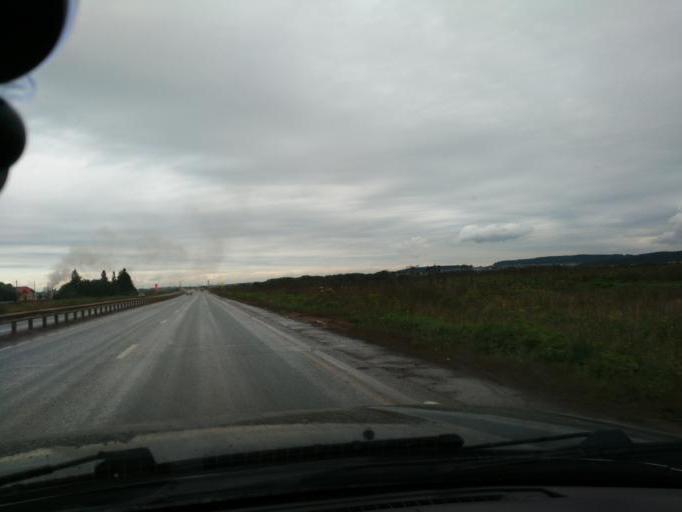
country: RU
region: Perm
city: Kultayevo
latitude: 57.8940
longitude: 55.9573
